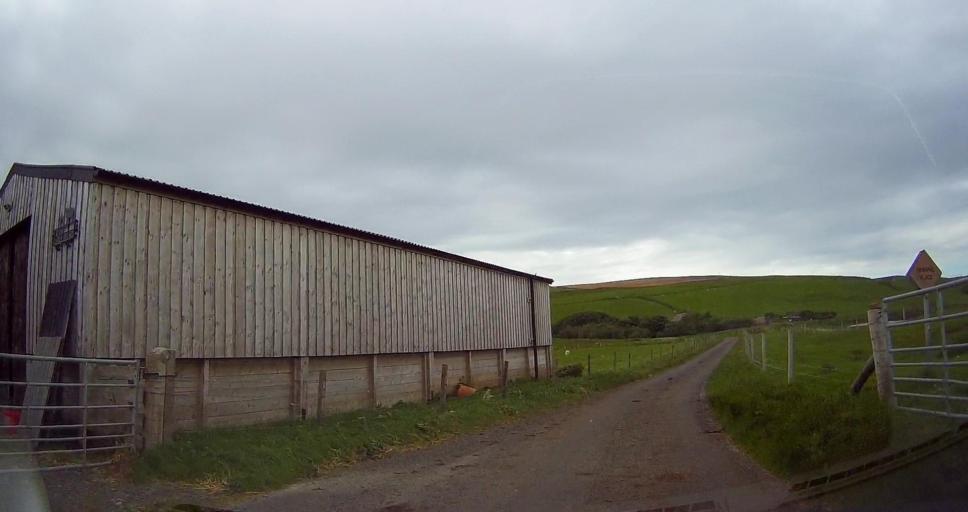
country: GB
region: Scotland
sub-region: Orkney Islands
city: Stromness
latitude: 58.9162
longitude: -3.3201
